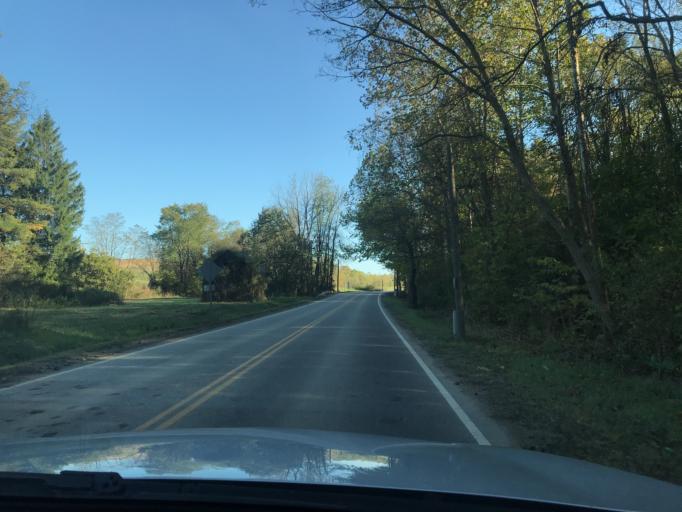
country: US
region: Ohio
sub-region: Pike County
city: Waverly
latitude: 39.0873
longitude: -82.9652
